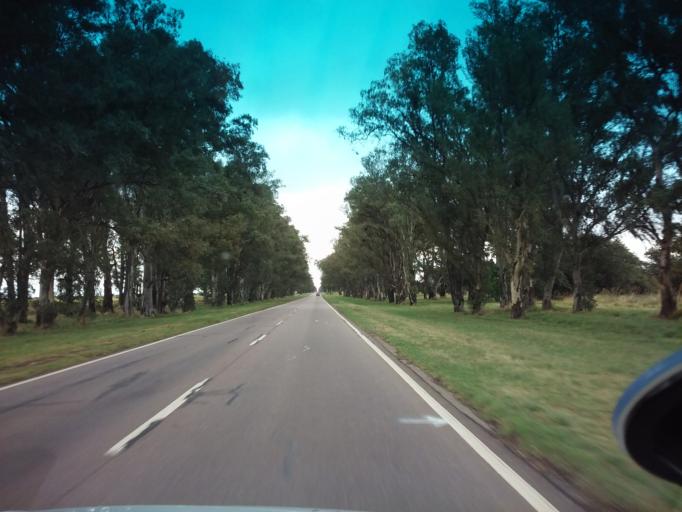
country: AR
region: La Pampa
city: Anguil
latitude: -36.5701
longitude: -64.1432
